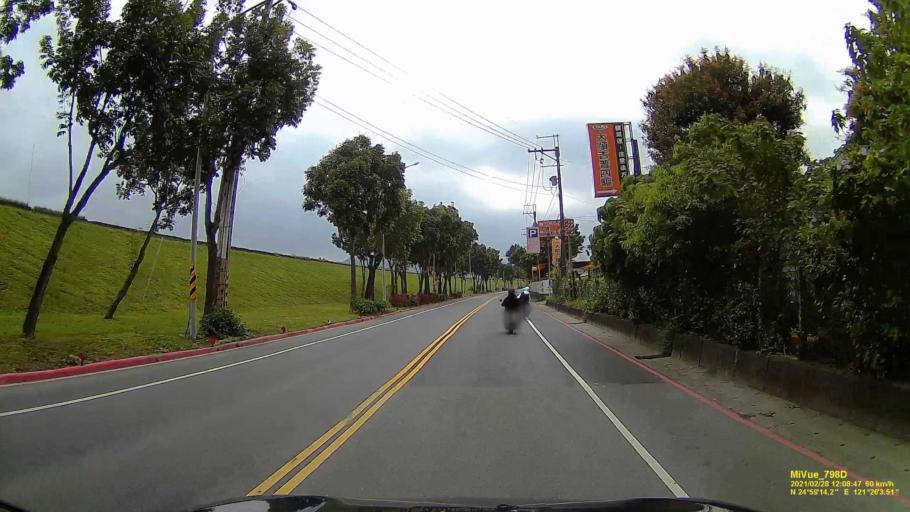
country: TW
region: Taipei
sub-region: Taipei
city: Banqiao
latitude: 24.9870
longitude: 121.4342
